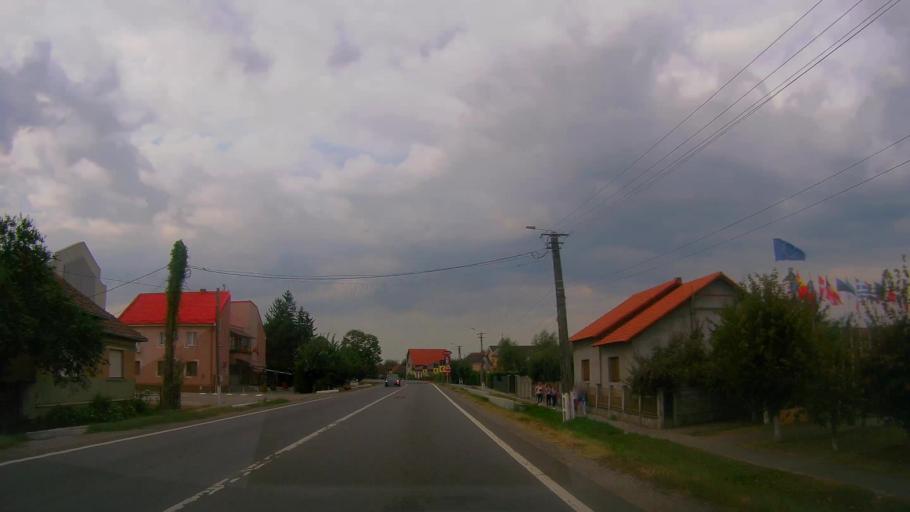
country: RO
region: Satu Mare
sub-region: Comuna Botiz
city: Botiz
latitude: 47.8329
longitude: 22.9546
